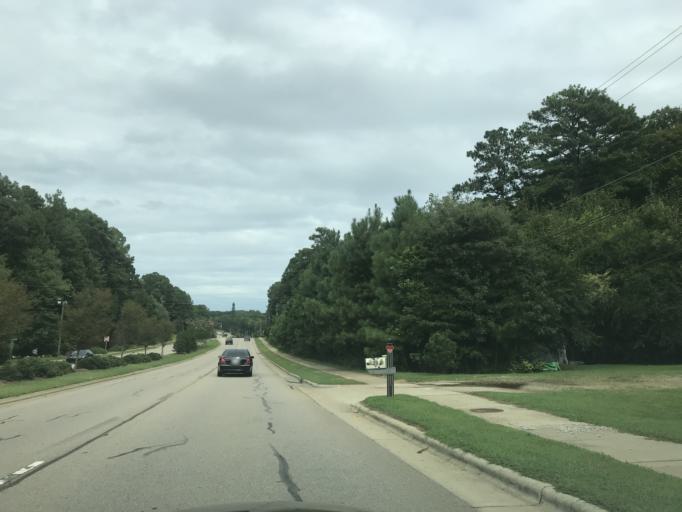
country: US
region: North Carolina
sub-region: Wake County
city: Cary
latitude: 35.7418
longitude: -78.7696
